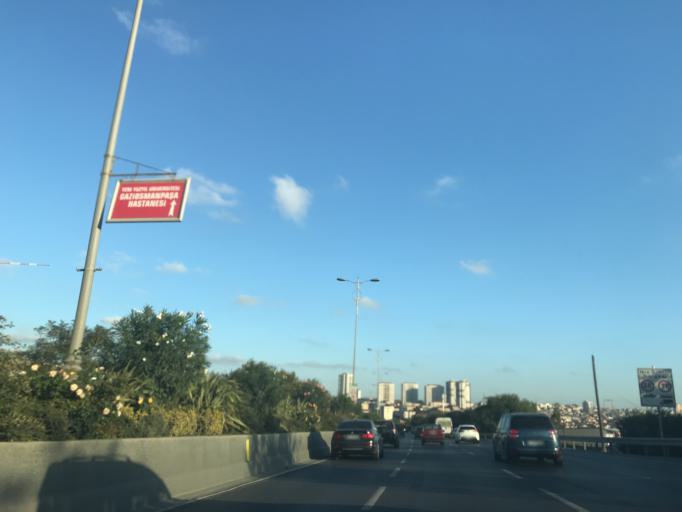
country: TR
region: Istanbul
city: Mahmutbey
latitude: 41.0586
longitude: 28.8453
